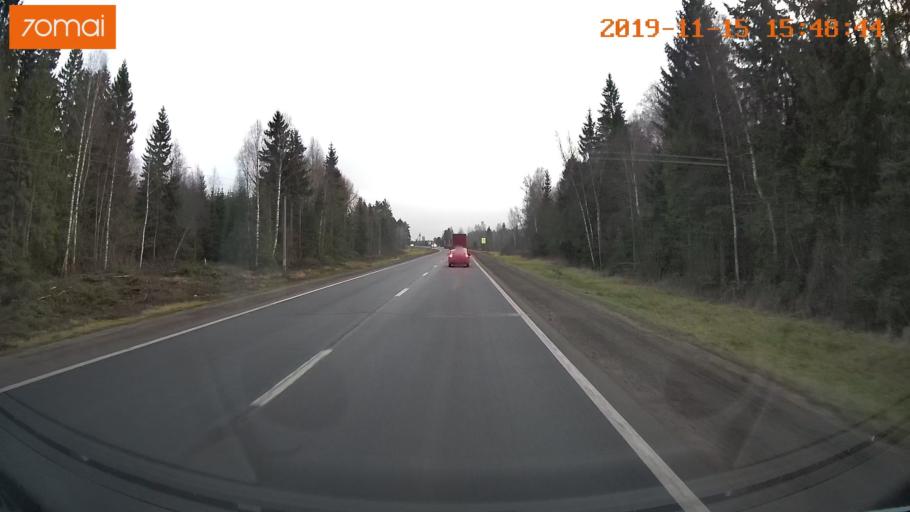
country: RU
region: Jaroslavl
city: Danilov
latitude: 57.9237
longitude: 40.0066
